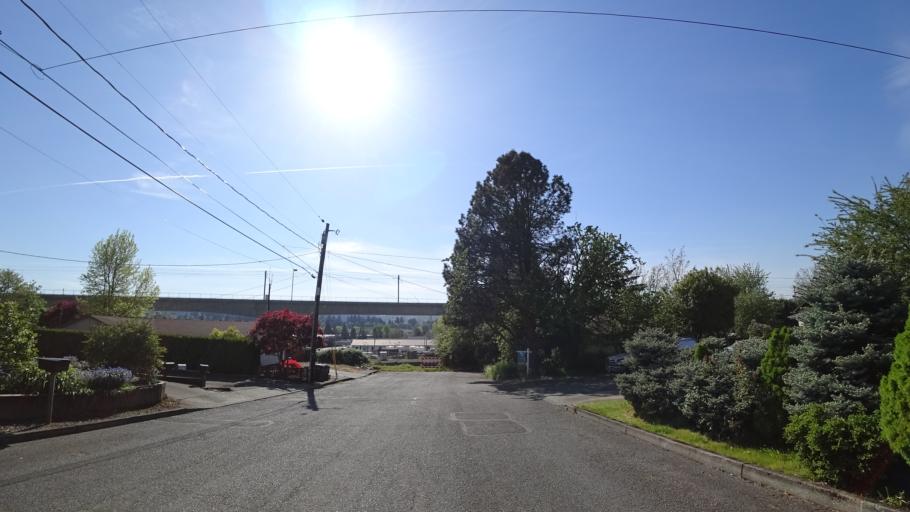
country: US
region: Oregon
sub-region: Clackamas County
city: Milwaukie
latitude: 45.4575
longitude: -122.6348
